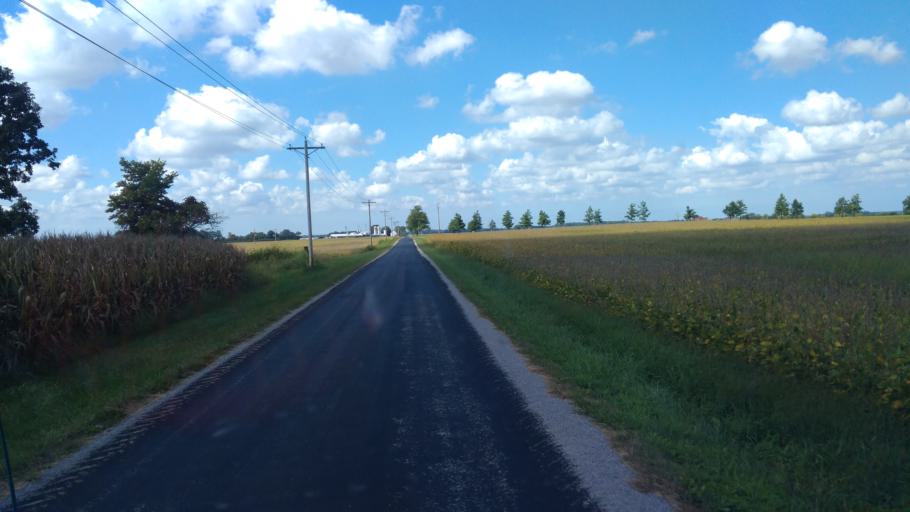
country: US
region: Ohio
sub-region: Marion County
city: Marion
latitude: 40.6587
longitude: -83.2619
